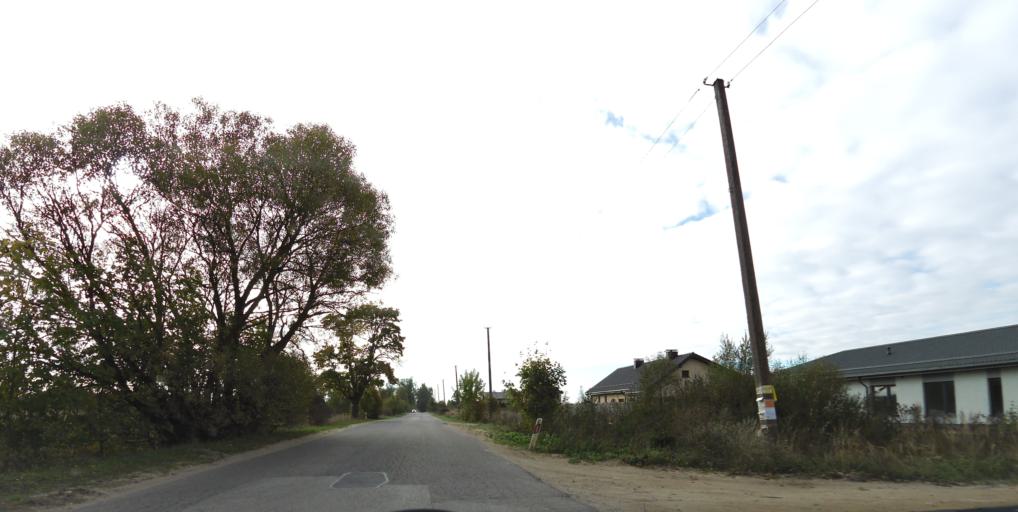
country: LT
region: Vilnius County
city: Pilaite
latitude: 54.7192
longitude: 25.1585
